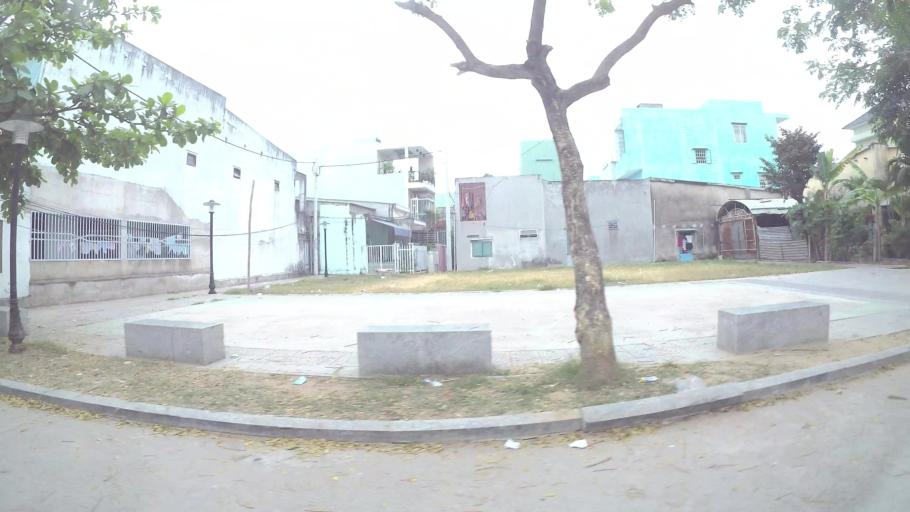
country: VN
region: Da Nang
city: Thanh Khe
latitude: 16.0588
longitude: 108.1891
